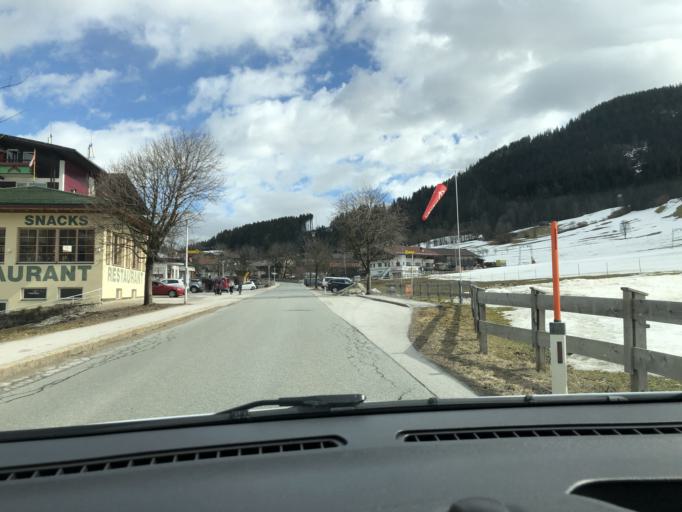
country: AT
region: Tyrol
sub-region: Politischer Bezirk Kitzbuhel
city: Itter
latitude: 47.4480
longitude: 12.0993
